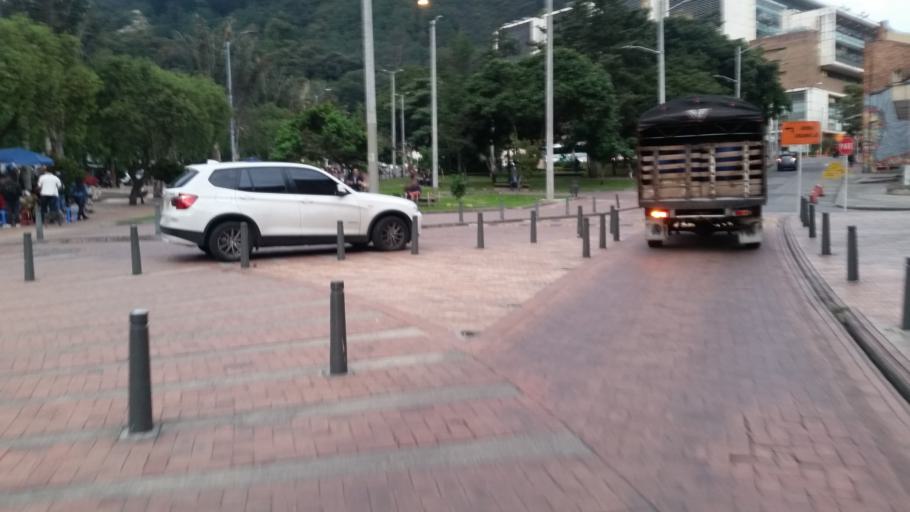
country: CO
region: Bogota D.C.
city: Bogota
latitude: 4.6030
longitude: -74.0663
